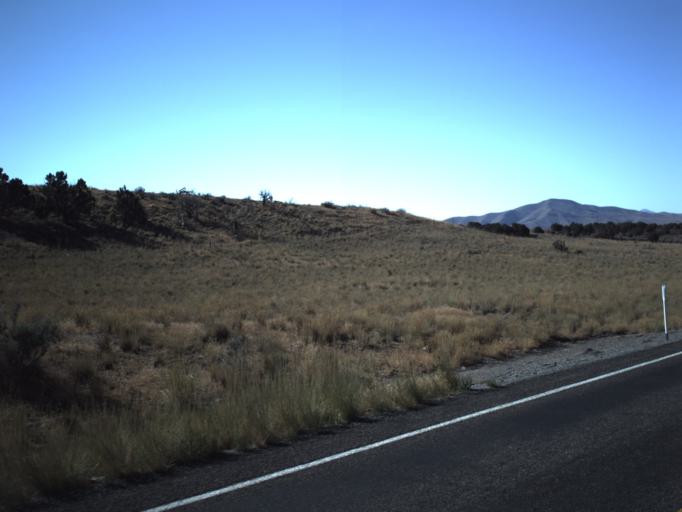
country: US
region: Utah
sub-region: Juab County
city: Mona
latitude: 39.7448
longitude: -112.1866
